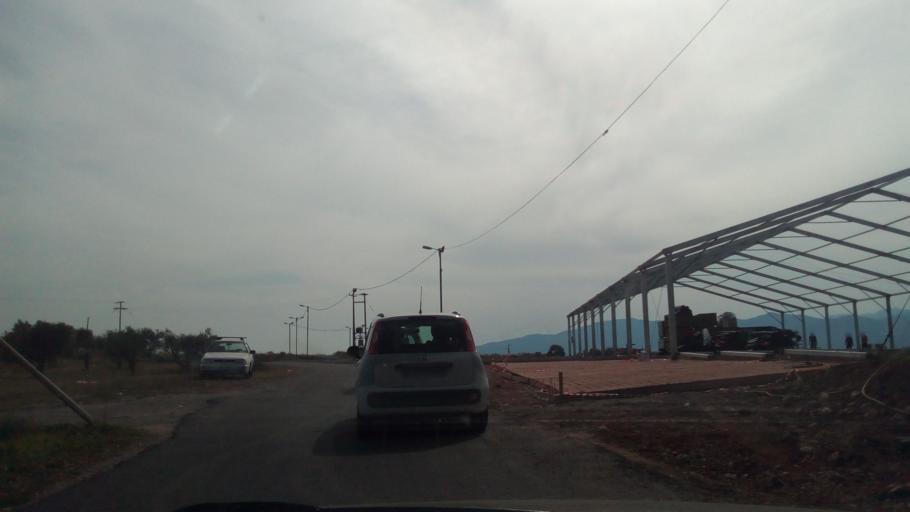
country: GR
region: West Greece
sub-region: Nomos Aitolias kai Akarnanias
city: Nafpaktos
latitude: 38.3892
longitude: 21.8423
